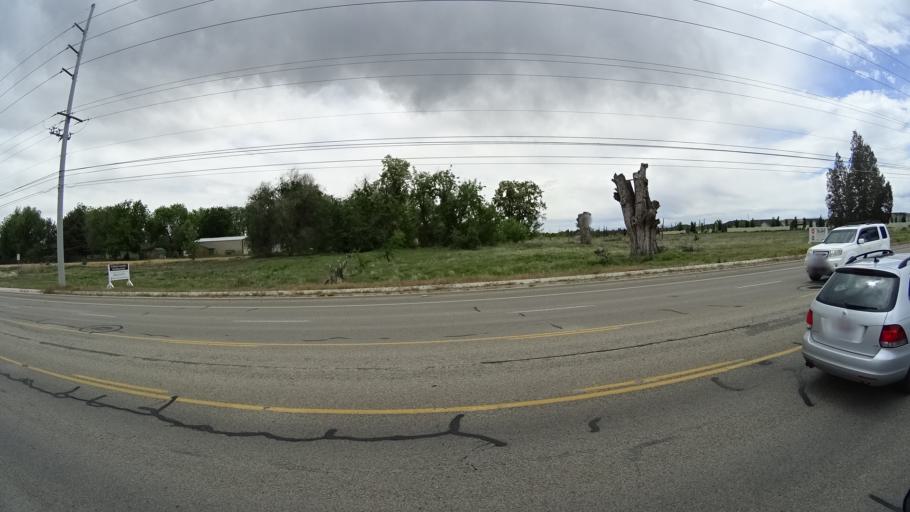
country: US
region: Idaho
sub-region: Ada County
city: Meridian
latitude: 43.5904
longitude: -116.3382
